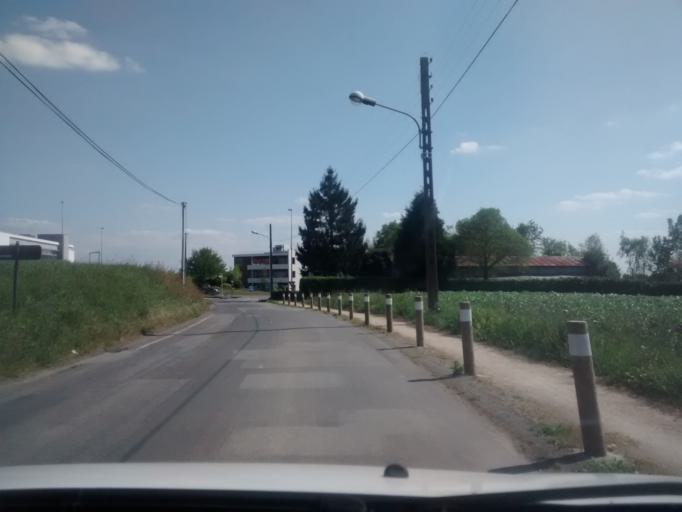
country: FR
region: Brittany
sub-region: Departement d'Ille-et-Vilaine
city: Cesson-Sevigne
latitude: 48.1327
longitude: -1.5977
